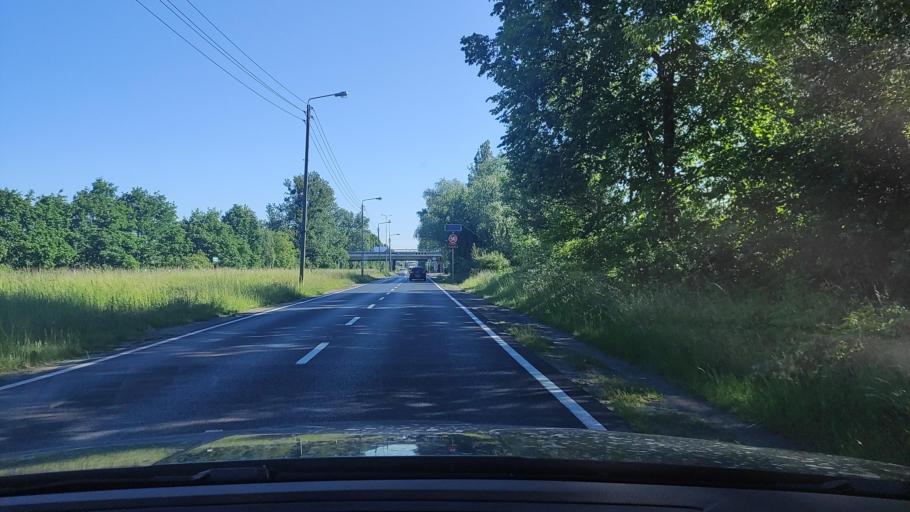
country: PL
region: Greater Poland Voivodeship
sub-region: Poznan
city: Poznan
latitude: 52.3806
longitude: 16.9279
